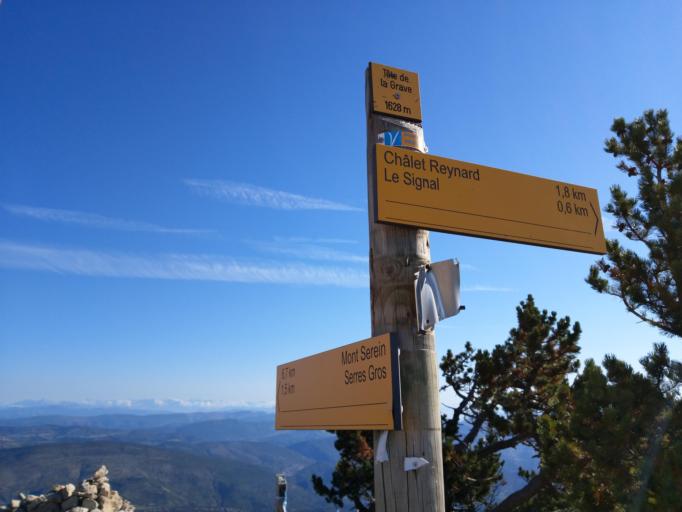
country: FR
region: Provence-Alpes-Cote d'Azur
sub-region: Departement du Vaucluse
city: Sault
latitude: 44.1620
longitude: 5.3155
